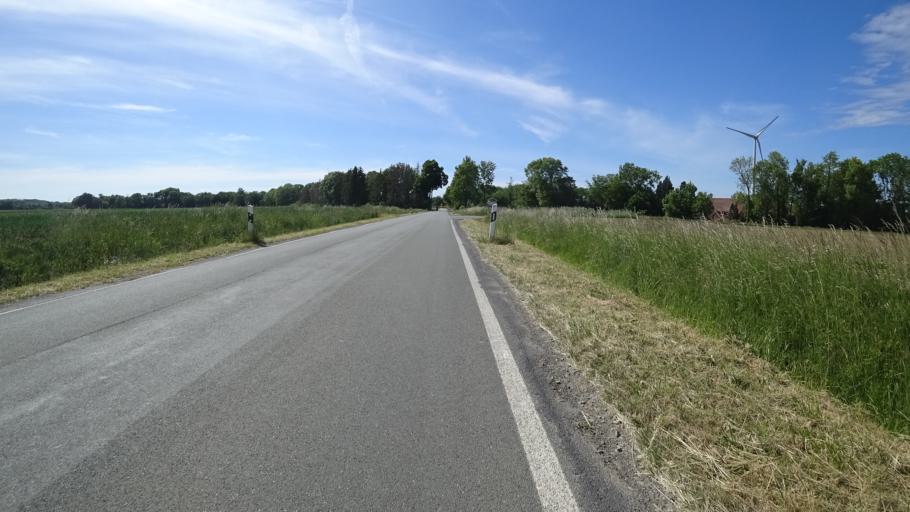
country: DE
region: North Rhine-Westphalia
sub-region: Regierungsbezirk Detmold
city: Rheda-Wiedenbruck
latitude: 51.8233
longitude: 8.2444
